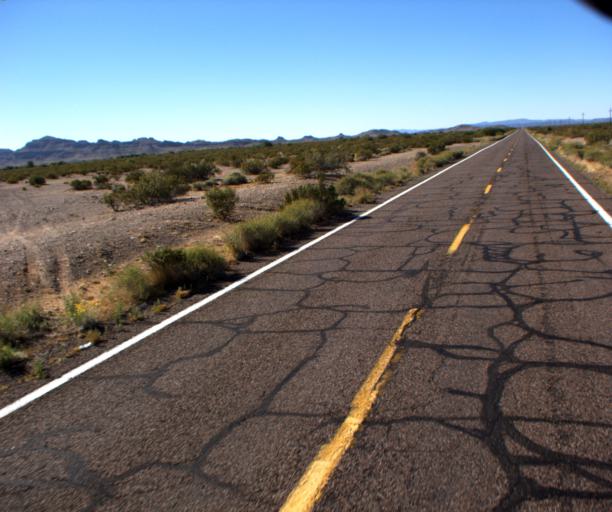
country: US
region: Arizona
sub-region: Maricopa County
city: Gila Bend
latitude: 32.7358
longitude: -112.8330
